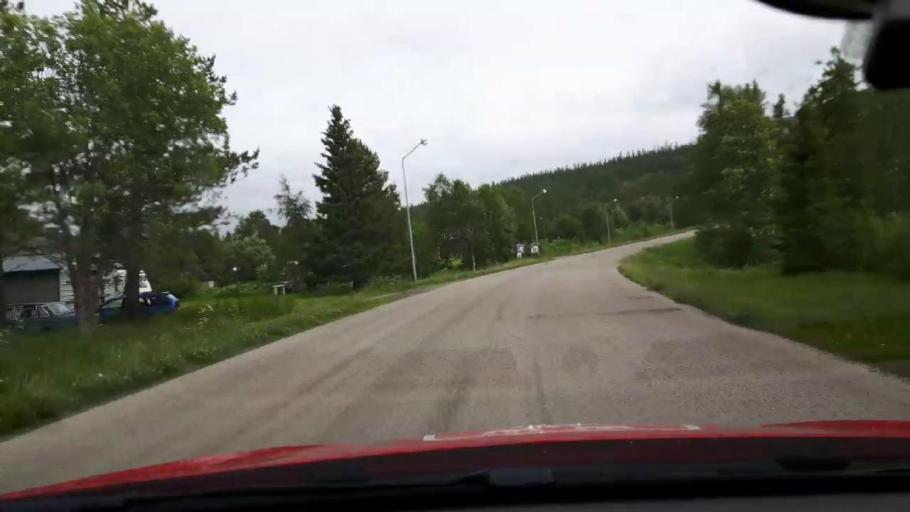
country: SE
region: Jaemtland
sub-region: Are Kommun
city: Are
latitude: 63.2564
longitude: 12.4527
